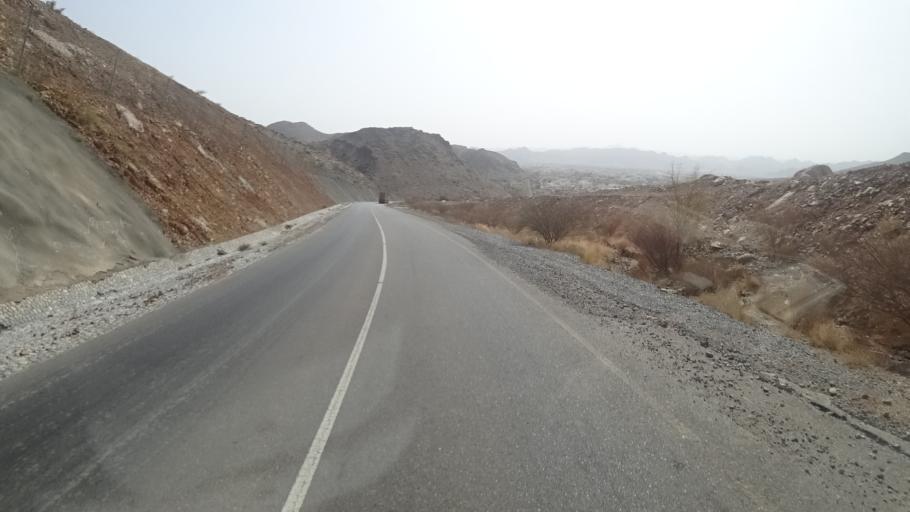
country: OM
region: Muhafazat ad Dakhiliyah
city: Nizwa
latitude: 23.0055
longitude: 57.5686
